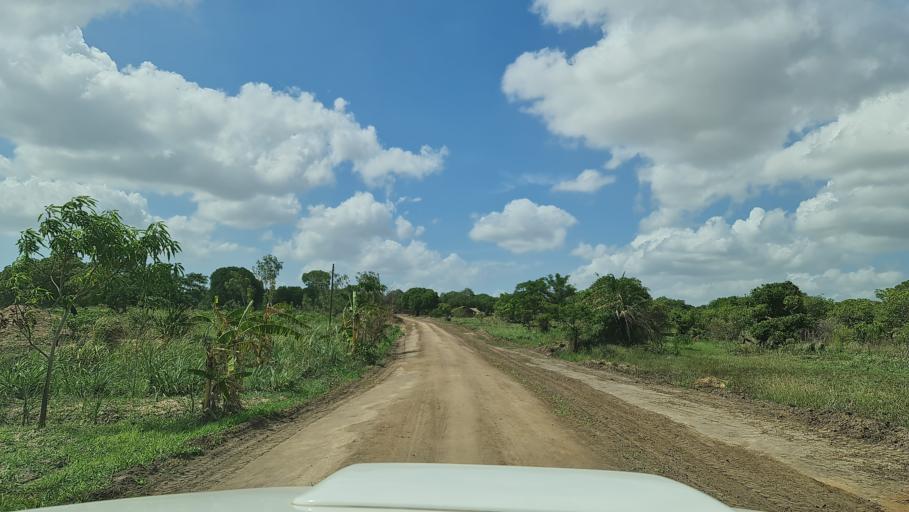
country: MZ
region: Nampula
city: Ilha de Mocambique
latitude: -15.0140
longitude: 40.5603
